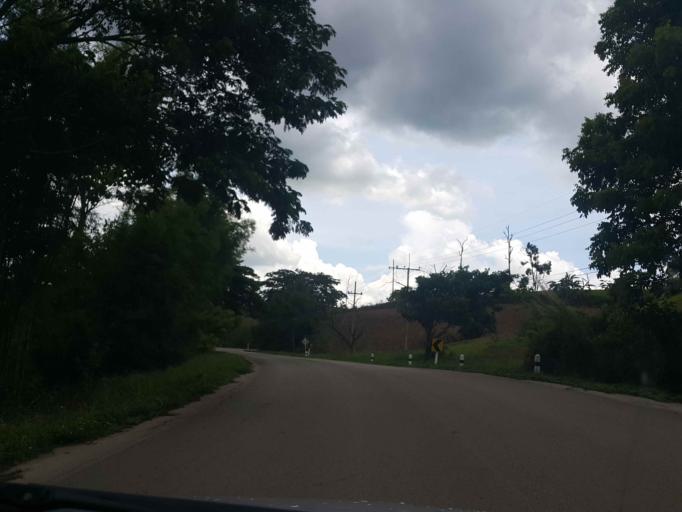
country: TH
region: Phayao
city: Dok Kham Tai
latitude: 18.9658
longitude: 100.0742
